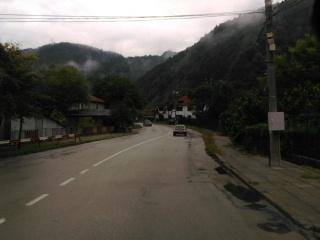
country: BG
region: Lovech
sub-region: Obshtina Troyan
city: Troyan
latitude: 42.8642
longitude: 24.6977
